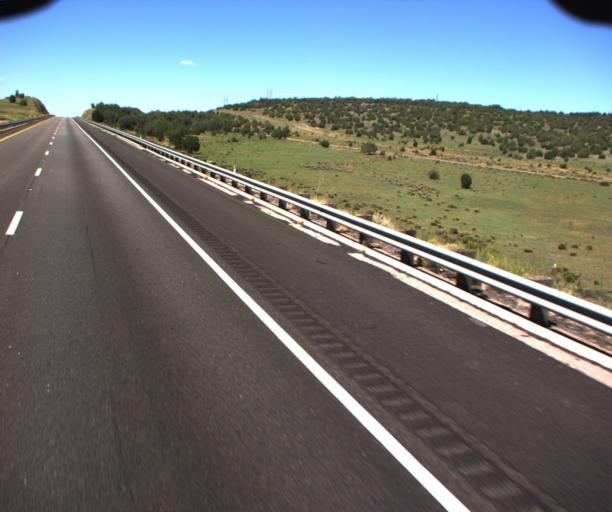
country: US
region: Arizona
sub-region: Mohave County
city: Peach Springs
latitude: 35.2444
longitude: -113.1937
